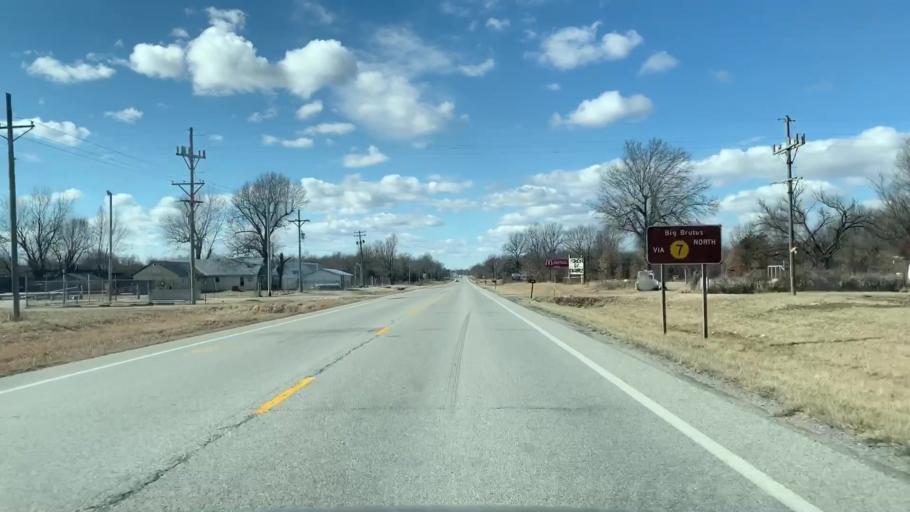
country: US
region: Kansas
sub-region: Cherokee County
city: Columbus
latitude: 37.1781
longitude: -94.8132
